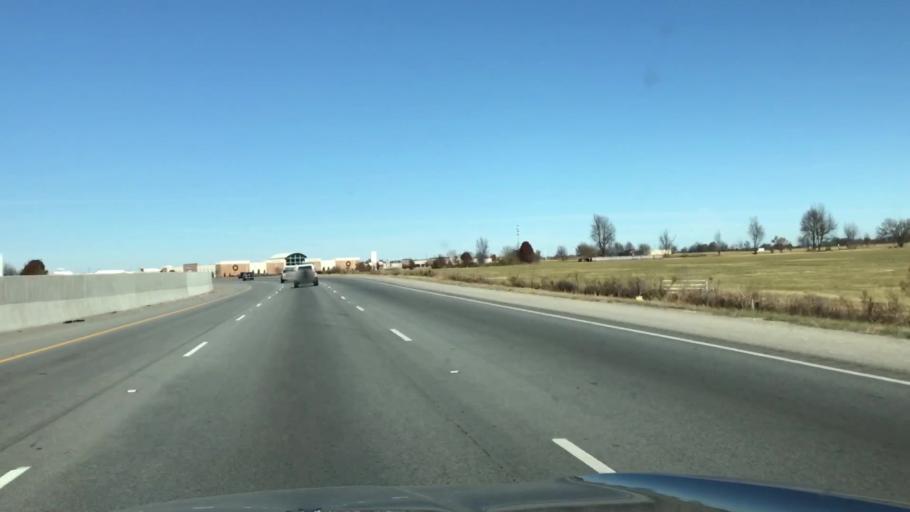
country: US
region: Arkansas
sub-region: Benton County
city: Lowell
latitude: 36.2714
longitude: -94.1508
